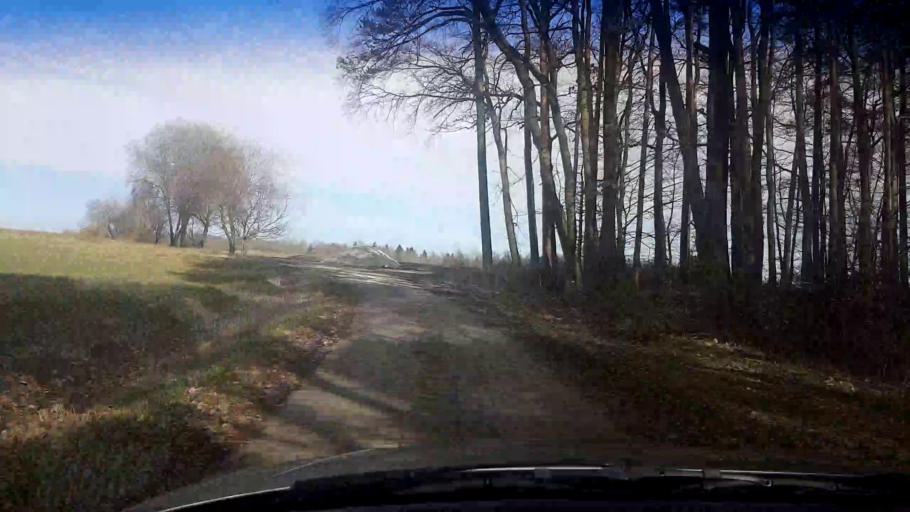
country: DE
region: Bavaria
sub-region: Upper Franconia
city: Burgebrach
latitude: 49.8060
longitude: 10.7419
